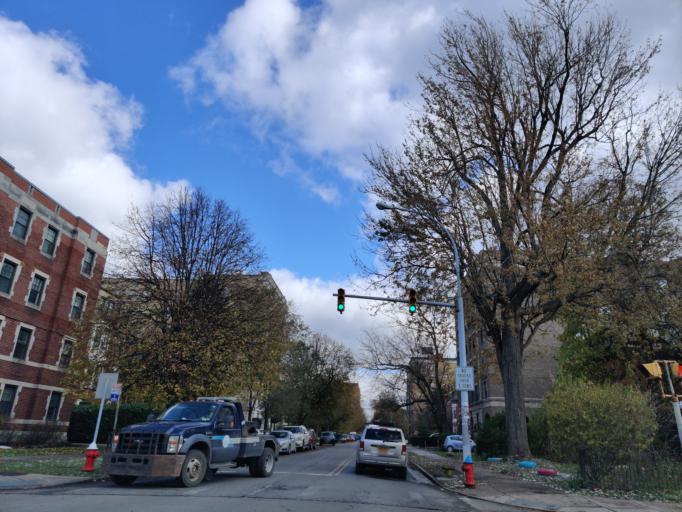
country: US
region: New York
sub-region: Erie County
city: Buffalo
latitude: 42.9022
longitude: -78.8772
